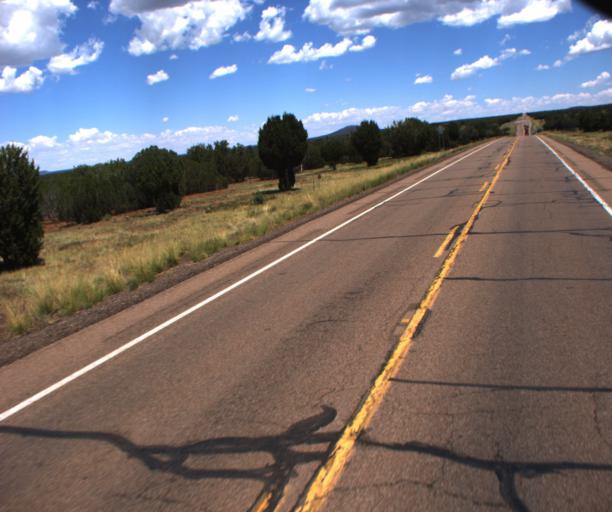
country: US
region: Arizona
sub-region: Navajo County
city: Show Low
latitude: 34.2675
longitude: -109.9422
